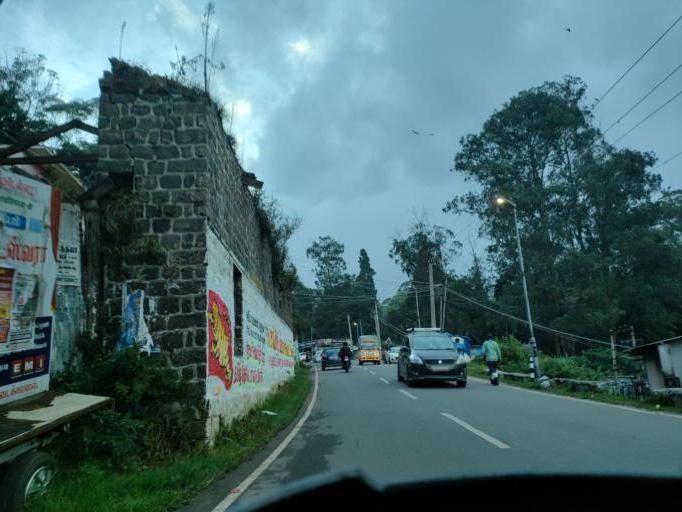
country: IN
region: Tamil Nadu
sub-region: Dindigul
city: Kodaikanal
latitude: 10.2383
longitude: 77.4905
